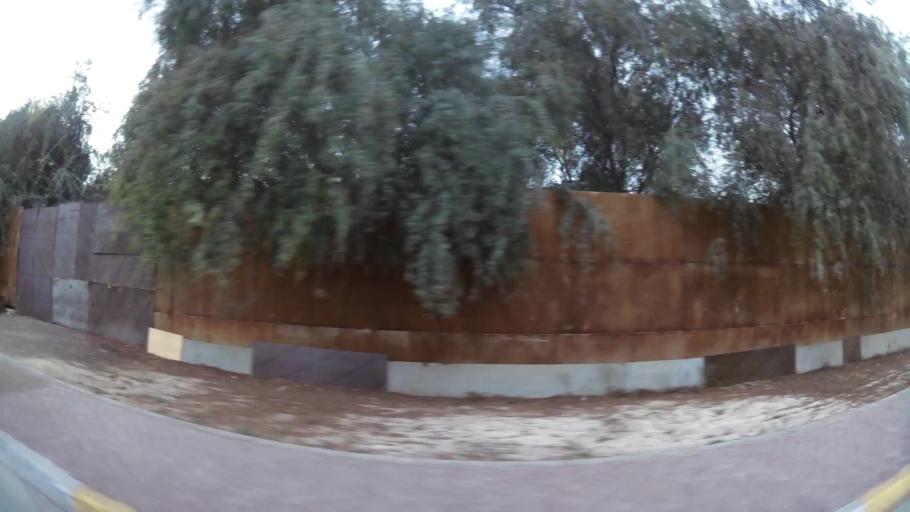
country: AE
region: Abu Dhabi
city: Abu Dhabi
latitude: 24.4765
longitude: 54.3584
